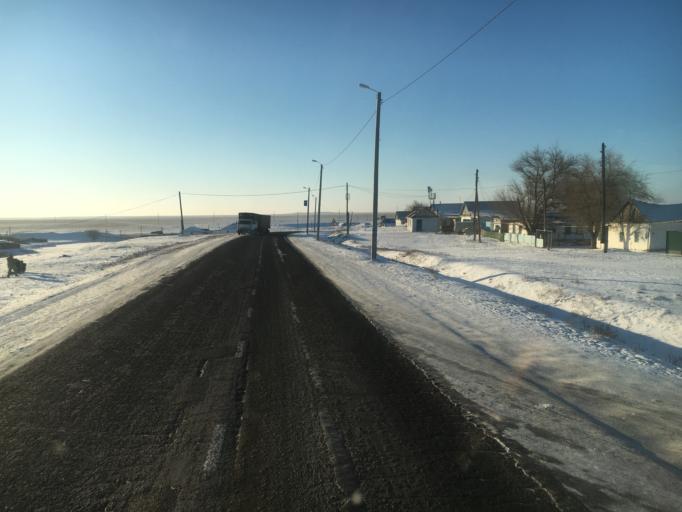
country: KZ
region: Aqtoebe
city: Khromtau
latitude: 50.1247
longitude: 59.0925
